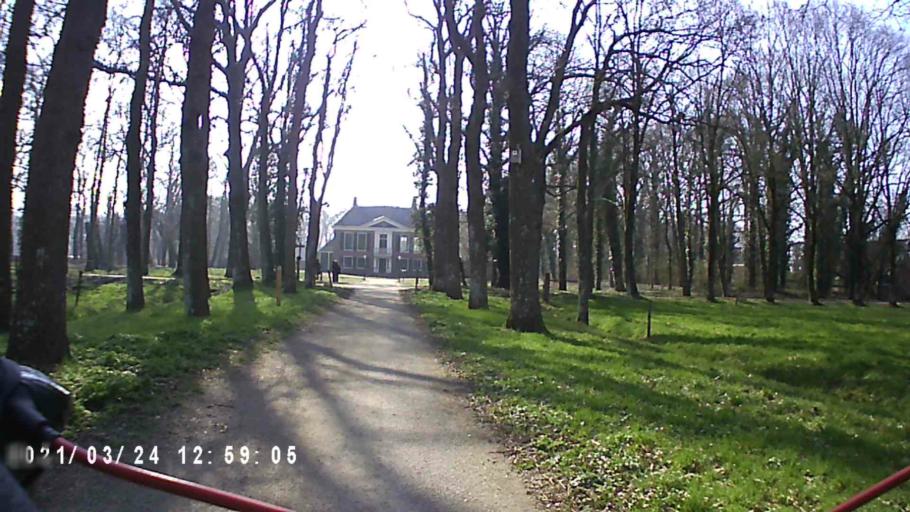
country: NL
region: Groningen
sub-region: Gemeente Grootegast
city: Grootegast
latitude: 53.1493
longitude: 6.3006
